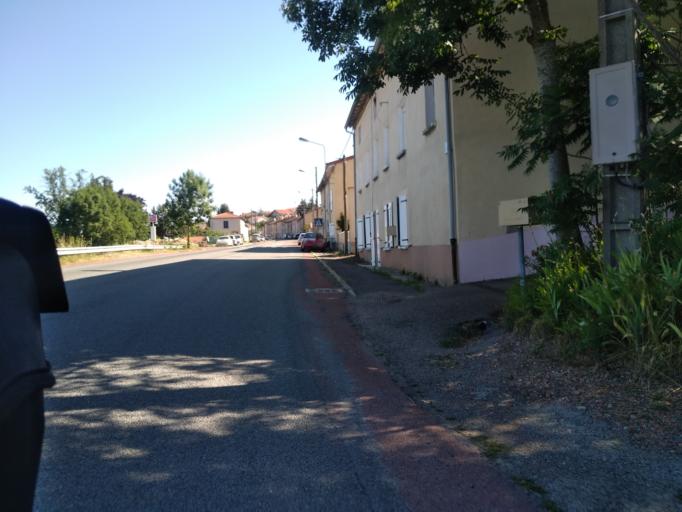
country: FR
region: Rhone-Alpes
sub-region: Departement de la Loire
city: Neulise
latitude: 45.8948
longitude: 4.1806
